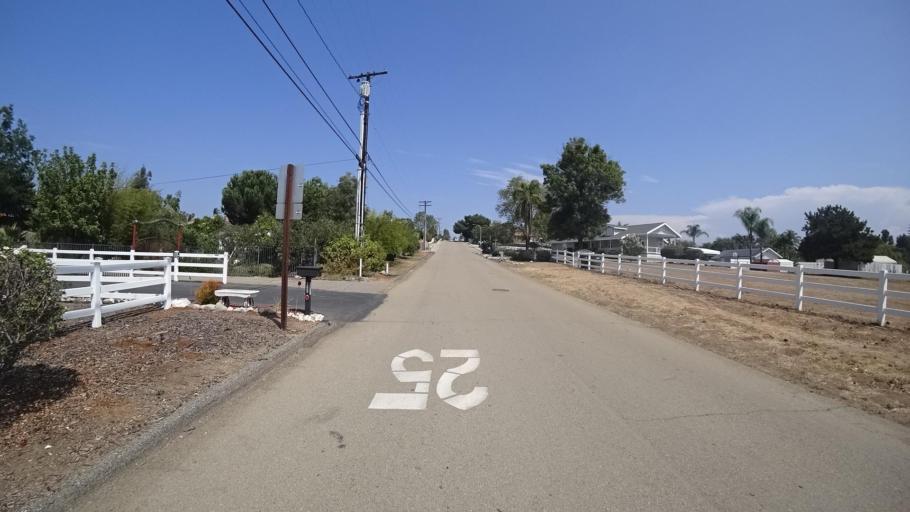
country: US
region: California
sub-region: San Diego County
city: Fallbrook
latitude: 33.3722
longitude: -117.2407
